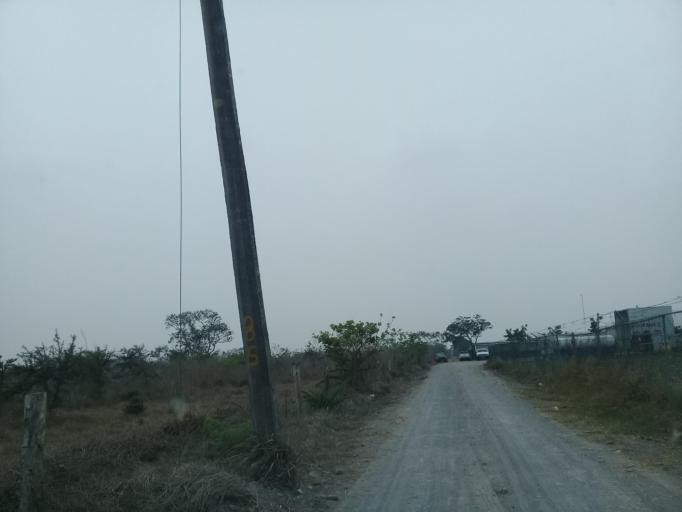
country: MX
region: Veracruz
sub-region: Medellin
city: La Laguna y Monte del Castillo
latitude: 18.9056
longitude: -96.1275
